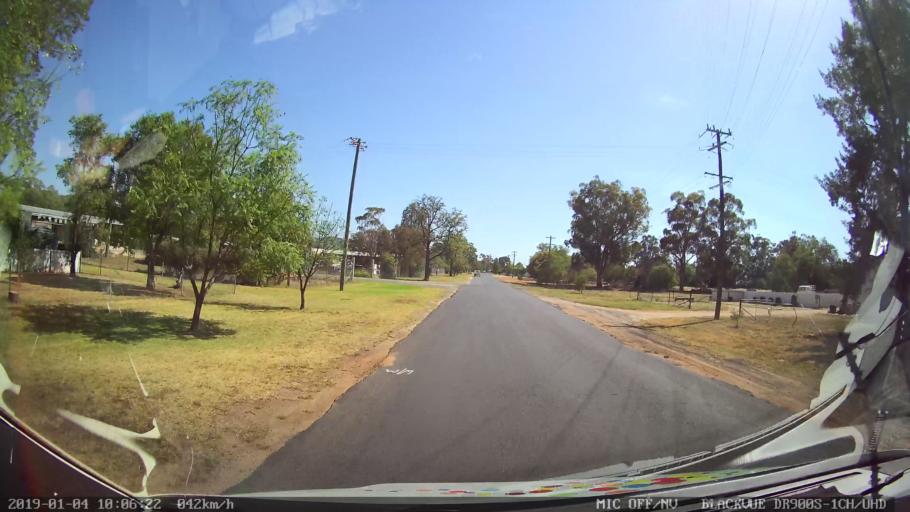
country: AU
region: New South Wales
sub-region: Cabonne
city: Canowindra
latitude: -33.4341
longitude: 148.3683
